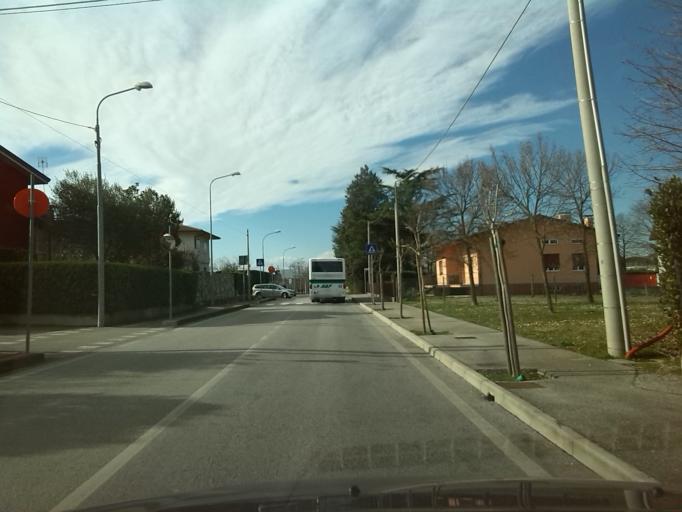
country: IT
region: Friuli Venezia Giulia
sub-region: Provincia di Udine
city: Corno di Rosazzo
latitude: 45.9753
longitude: 13.4519
